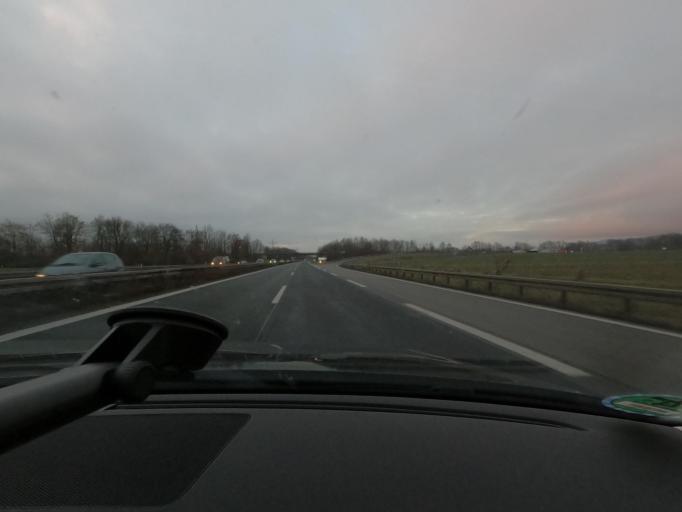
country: DE
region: Bavaria
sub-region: Upper Franconia
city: Buttenheim
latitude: 49.7935
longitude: 11.0276
